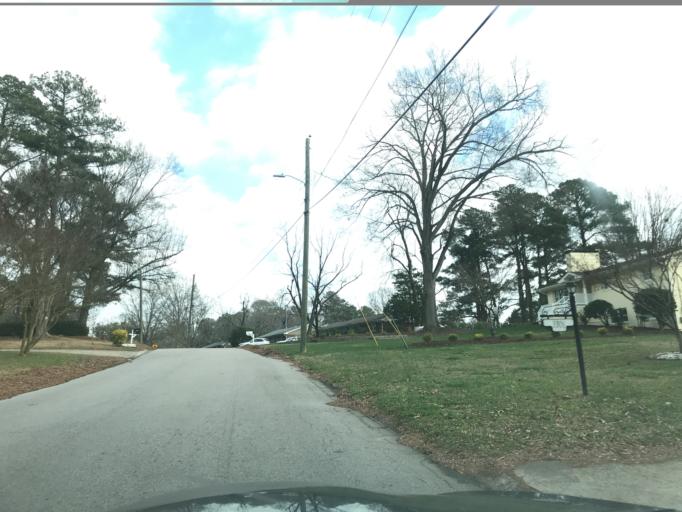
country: US
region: North Carolina
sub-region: Wake County
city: Raleigh
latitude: 35.8231
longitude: -78.5828
